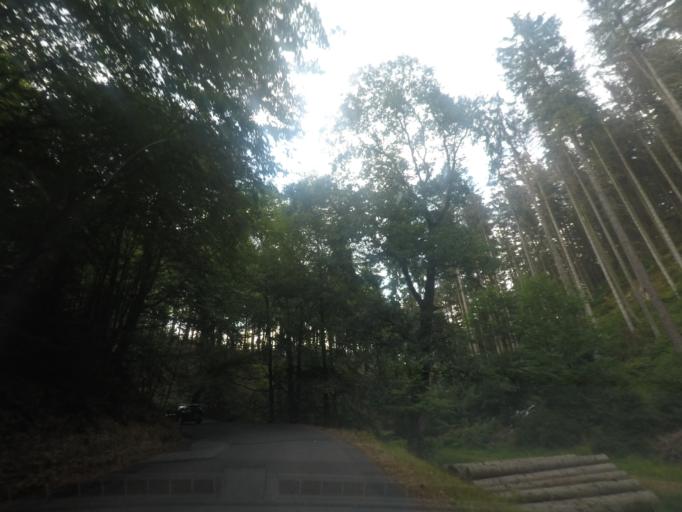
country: CZ
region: Ustecky
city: Mikulasovice
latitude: 50.8662
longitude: 14.3336
